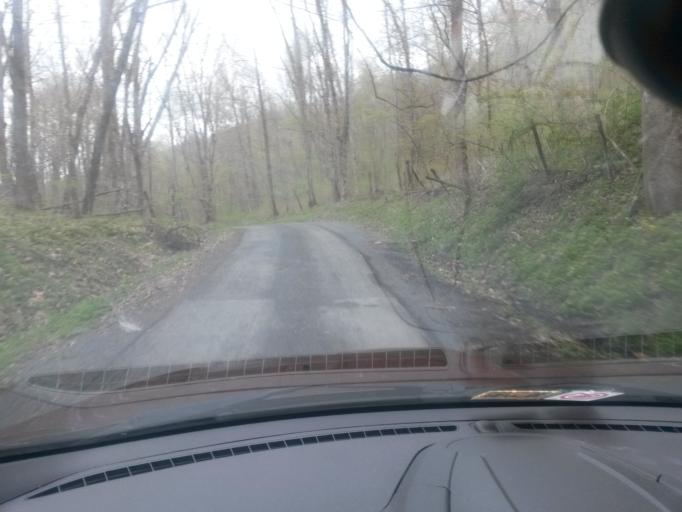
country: US
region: West Virginia
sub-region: Nicholas County
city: Richwood
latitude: 38.0616
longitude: -80.3392
